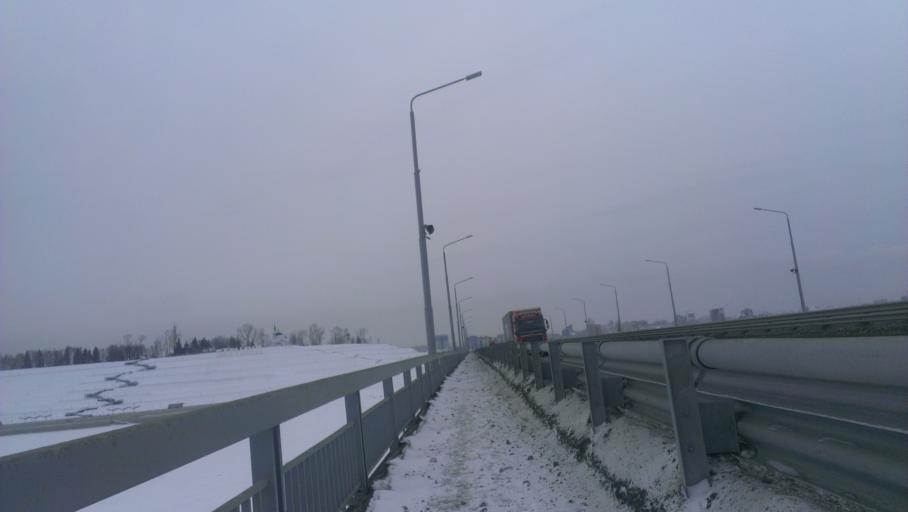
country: RU
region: Altai Krai
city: Zaton
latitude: 53.3220
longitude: 83.8071
